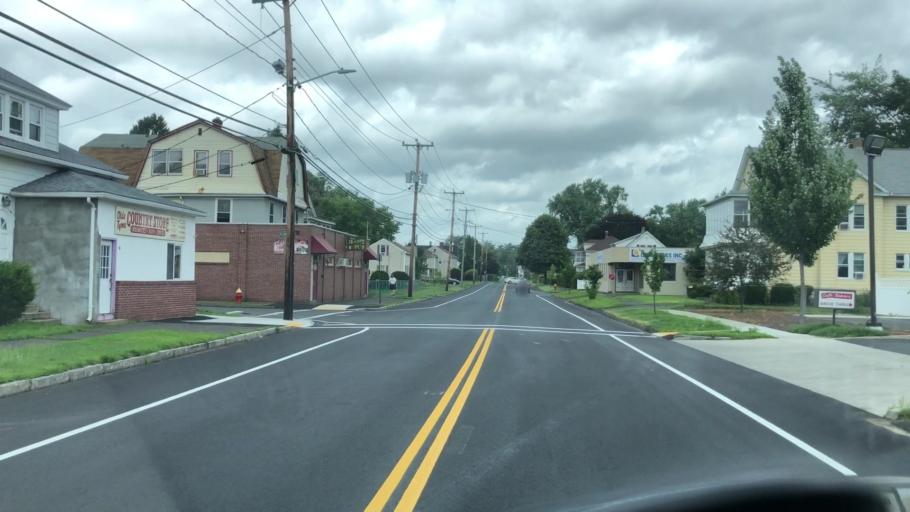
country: US
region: Massachusetts
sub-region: Hampden County
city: Chicopee
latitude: 42.1610
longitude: -72.6148
